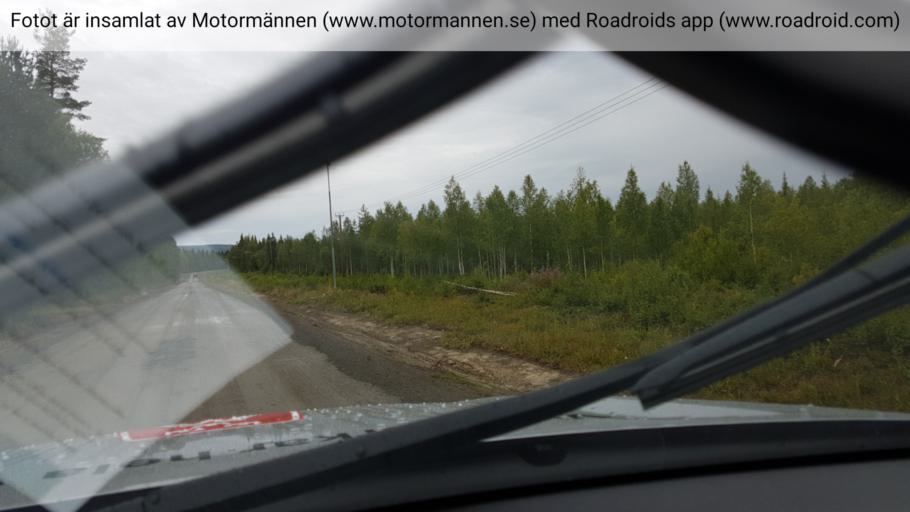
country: SE
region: Norrbotten
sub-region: Alvsbyns Kommun
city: AElvsbyn
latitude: 65.9128
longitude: 21.2794
